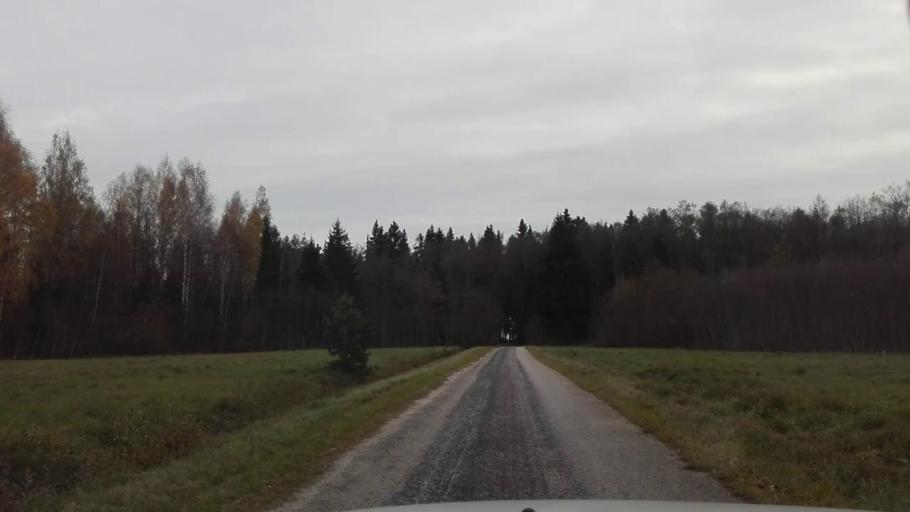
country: EE
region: Jogevamaa
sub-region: Poltsamaa linn
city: Poltsamaa
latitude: 58.4091
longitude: 26.0099
